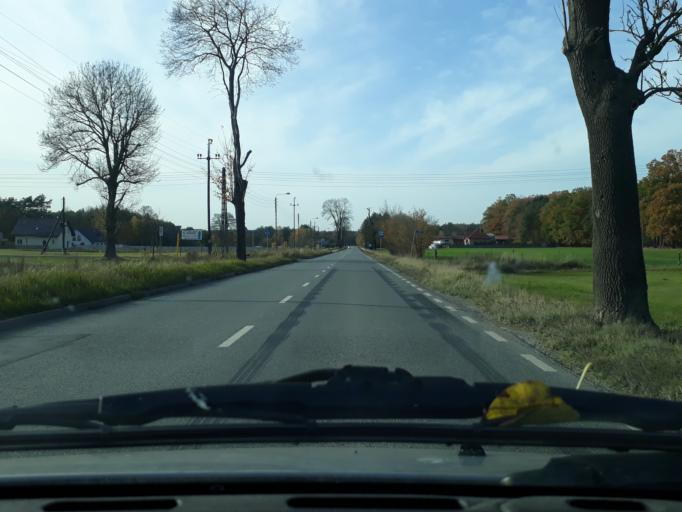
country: PL
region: Silesian Voivodeship
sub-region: Powiat lubliniecki
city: Psary
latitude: 50.5766
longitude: 18.9827
